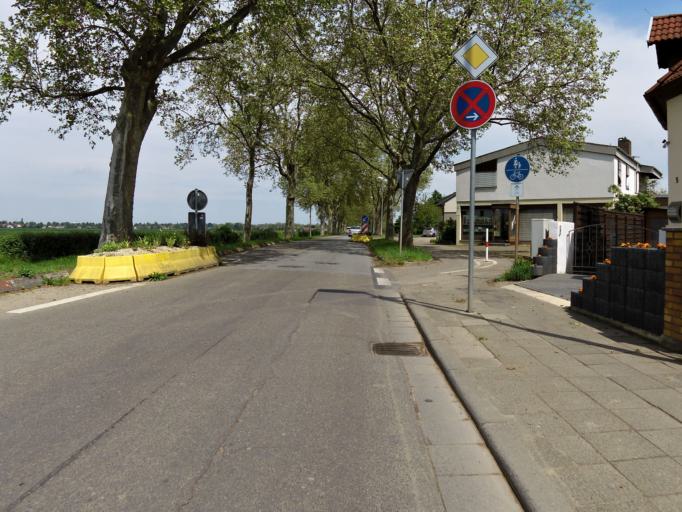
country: DE
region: Rheinland-Pfalz
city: Frankenthal
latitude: 49.5171
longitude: 8.3355
